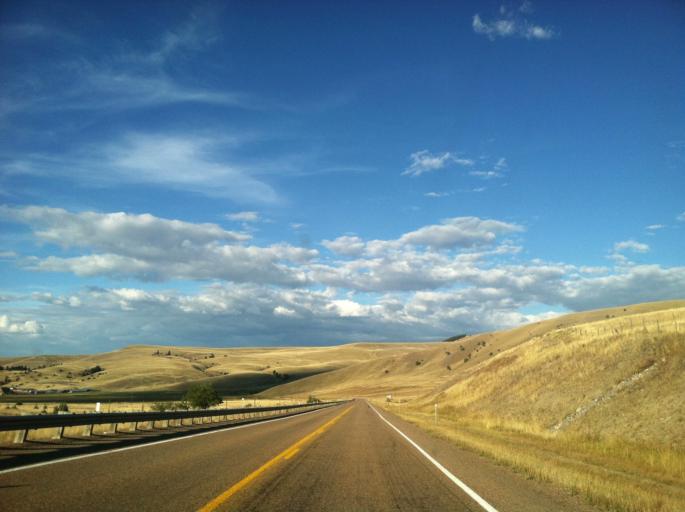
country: US
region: Montana
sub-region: Granite County
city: Philipsburg
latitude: 46.4892
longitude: -113.2290
